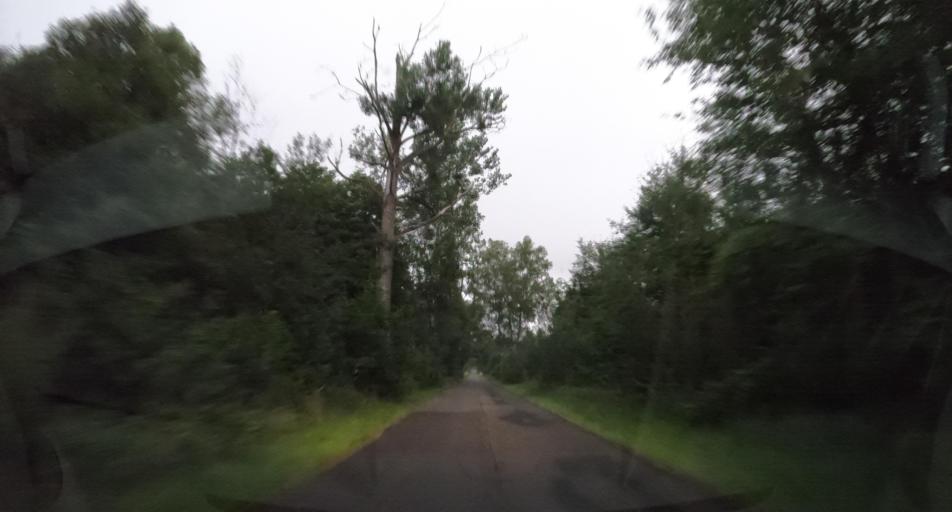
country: PL
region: West Pomeranian Voivodeship
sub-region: Powiat lobeski
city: Resko
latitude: 53.7575
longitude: 15.4226
